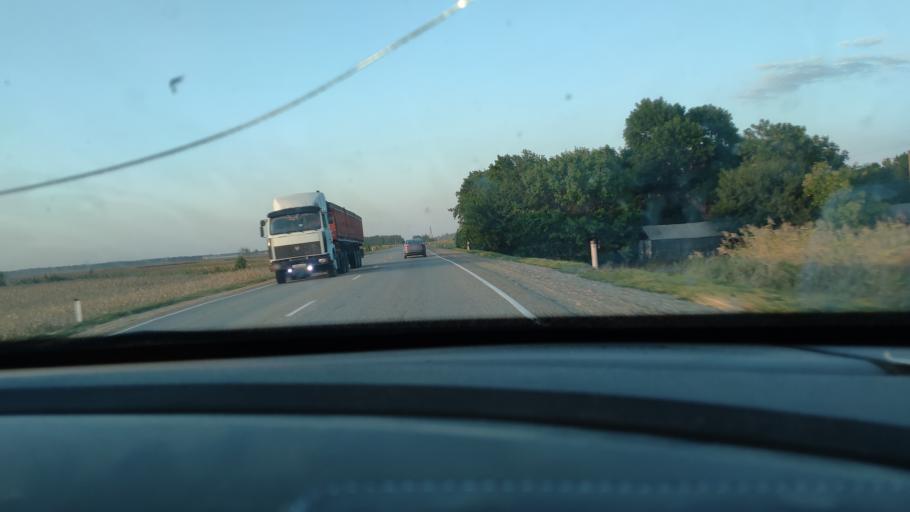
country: RU
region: Krasnodarskiy
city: Starominskaya
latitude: 46.4295
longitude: 39.0146
